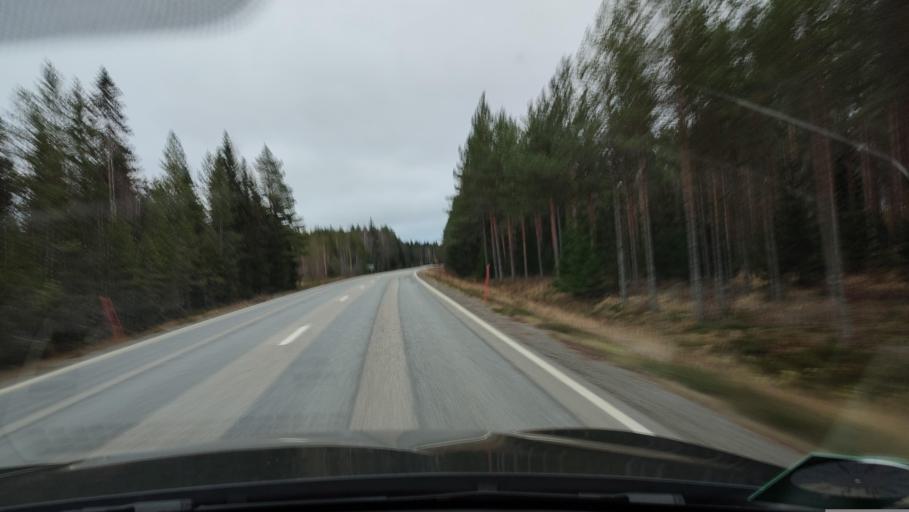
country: FI
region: Southern Ostrobothnia
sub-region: Suupohja
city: Karijoki
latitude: 62.2320
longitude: 21.7249
